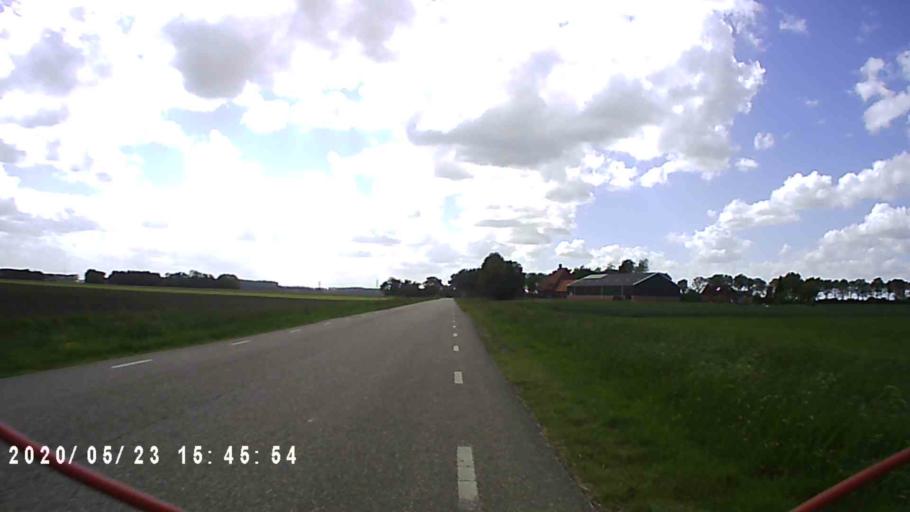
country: NL
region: Groningen
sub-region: Gemeente Delfzijl
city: Delfzijl
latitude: 53.2797
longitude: 6.9142
